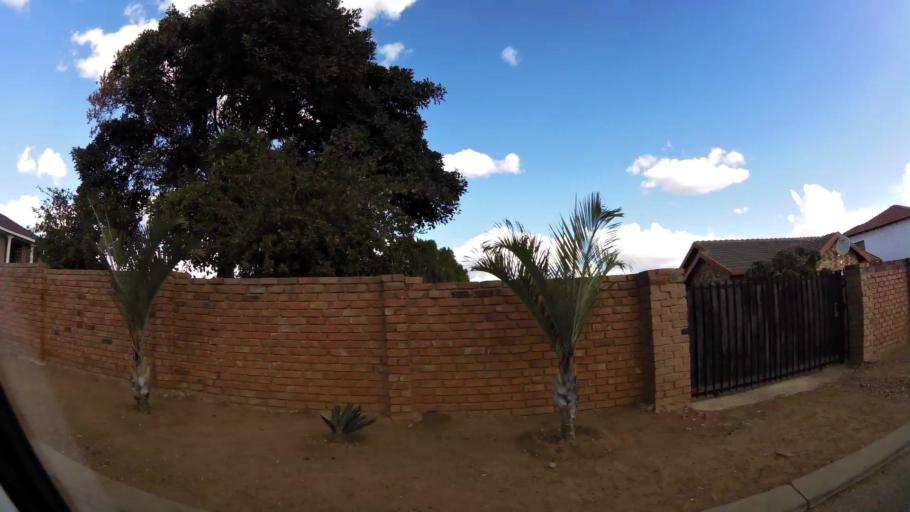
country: ZA
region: Limpopo
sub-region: Capricorn District Municipality
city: Polokwane
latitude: -23.9141
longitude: 29.5008
